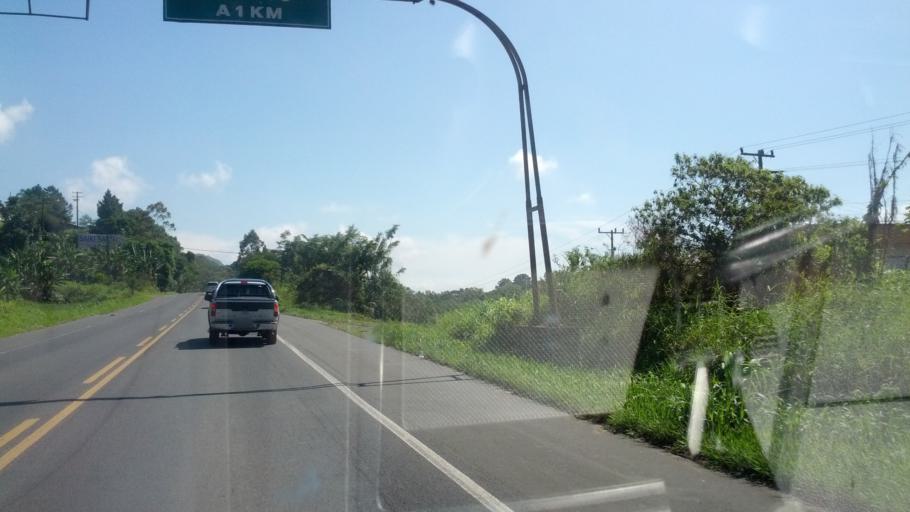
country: BR
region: Santa Catarina
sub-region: Rio Do Sul
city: Rio do Sul
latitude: -27.2273
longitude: -49.6671
